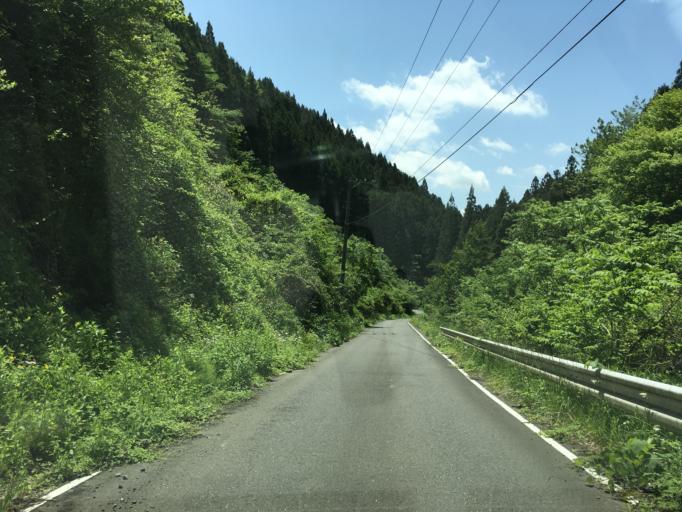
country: JP
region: Miyagi
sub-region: Oshika Gun
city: Onagawa Cho
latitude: 38.6769
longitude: 141.3477
